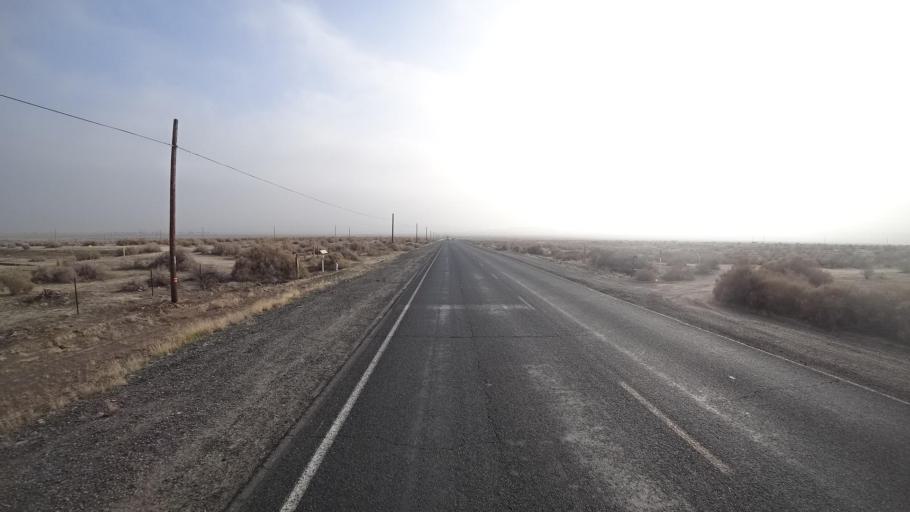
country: US
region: California
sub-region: Kern County
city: Ford City
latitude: 35.2293
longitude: -119.4456
